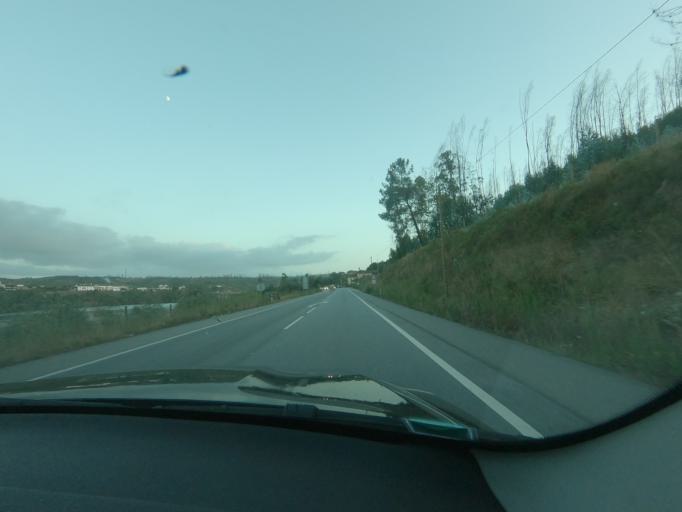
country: PT
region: Viseu
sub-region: Mortagua
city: Mortagua
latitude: 40.3261
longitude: -8.2299
